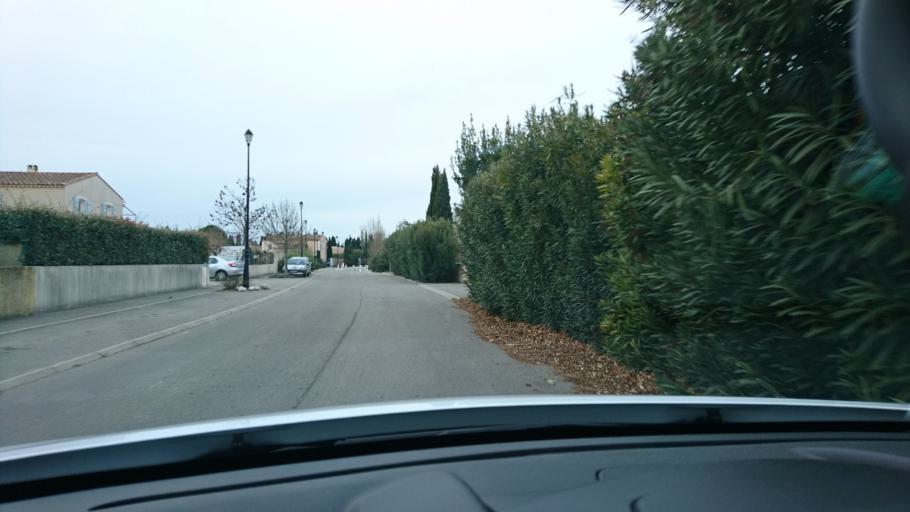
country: FR
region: Provence-Alpes-Cote d'Azur
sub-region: Departement des Bouches-du-Rhone
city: Rognonas
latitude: 43.9032
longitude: 4.8000
